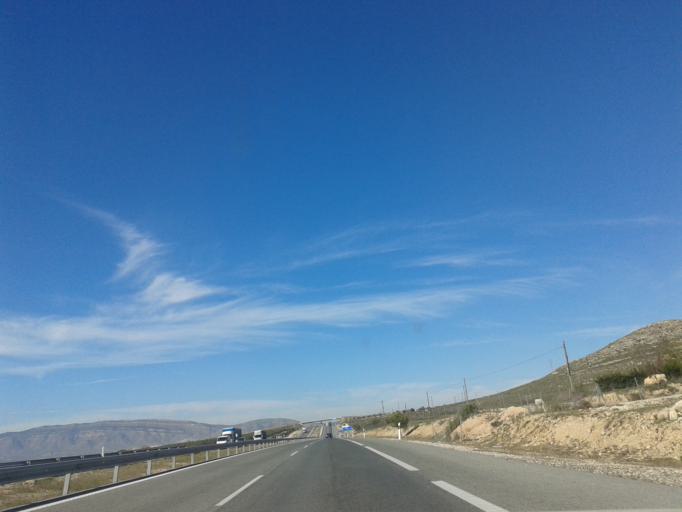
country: ES
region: Valencia
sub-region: Provincia de Alicante
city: Villena
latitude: 38.6901
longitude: -0.9088
